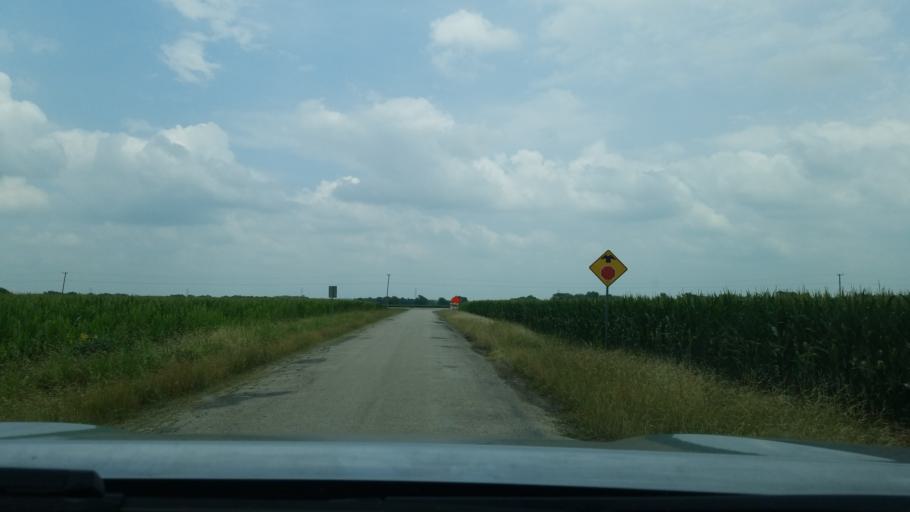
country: US
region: Texas
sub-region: Guadalupe County
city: Geronimo
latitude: 29.6802
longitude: -98.0050
